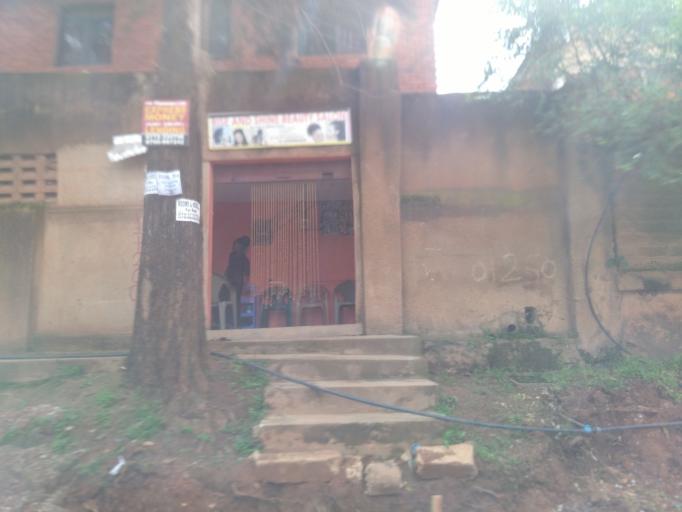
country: UG
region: Central Region
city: Kampala Central Division
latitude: 0.3450
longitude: 32.5651
